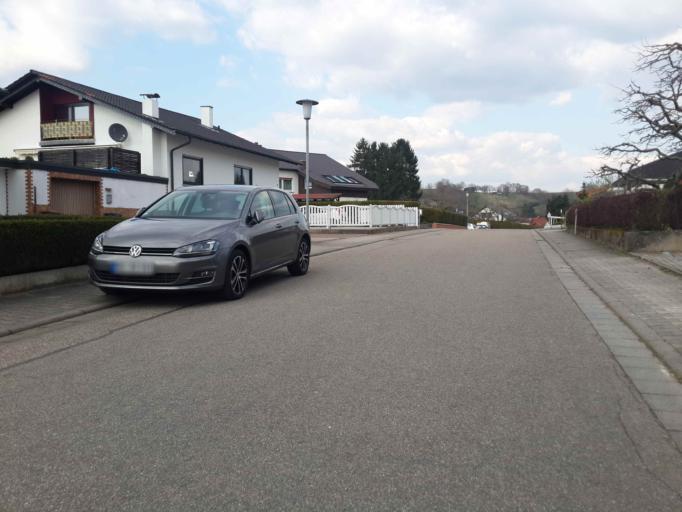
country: DE
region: Baden-Wuerttemberg
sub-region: Karlsruhe Region
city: Balzfeld
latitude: 49.2456
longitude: 8.7833
